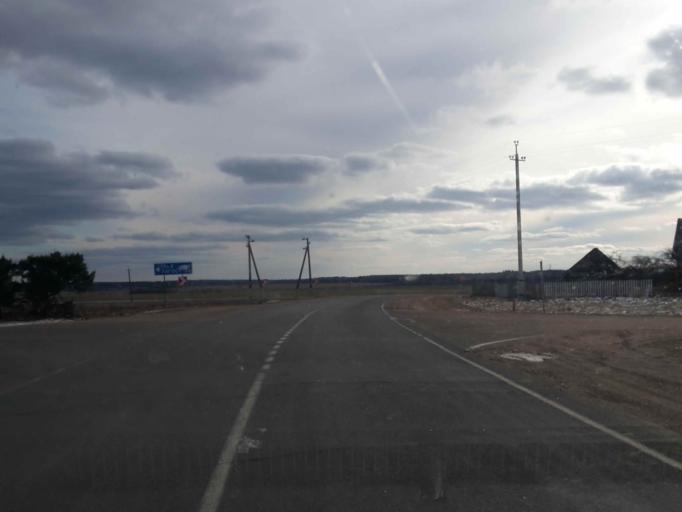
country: BY
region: Minsk
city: Il'ya
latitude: 54.4344
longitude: 27.2847
